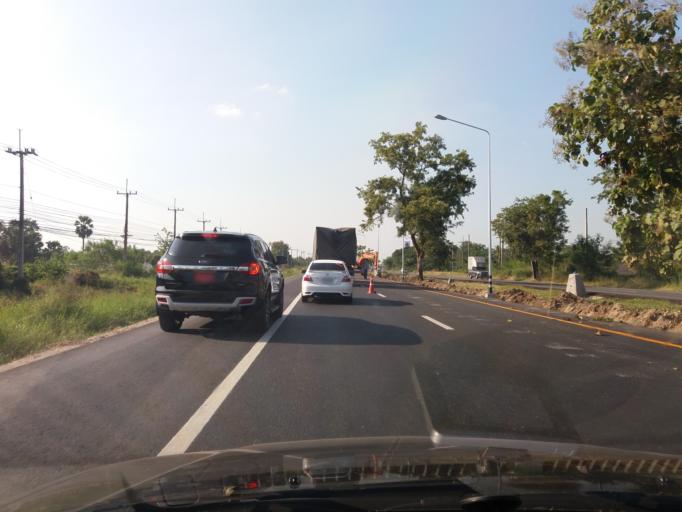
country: TH
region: Nakhon Sawan
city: Banphot Phisai
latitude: 15.8120
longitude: 99.9463
